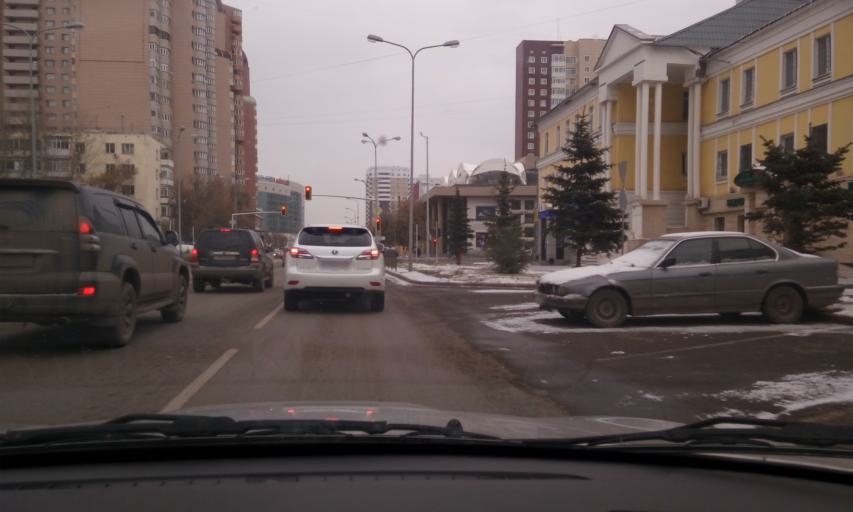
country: KZ
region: Astana Qalasy
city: Astana
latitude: 51.1637
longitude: 71.4369
